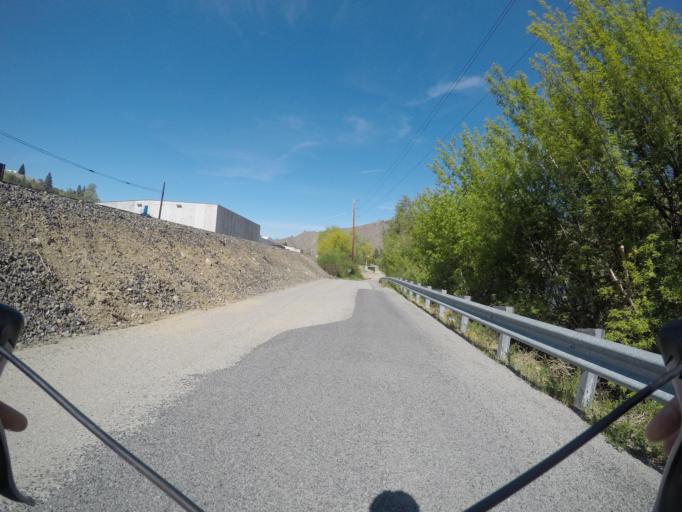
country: US
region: Washington
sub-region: Chelan County
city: Cashmere
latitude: 47.5158
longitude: -120.4575
